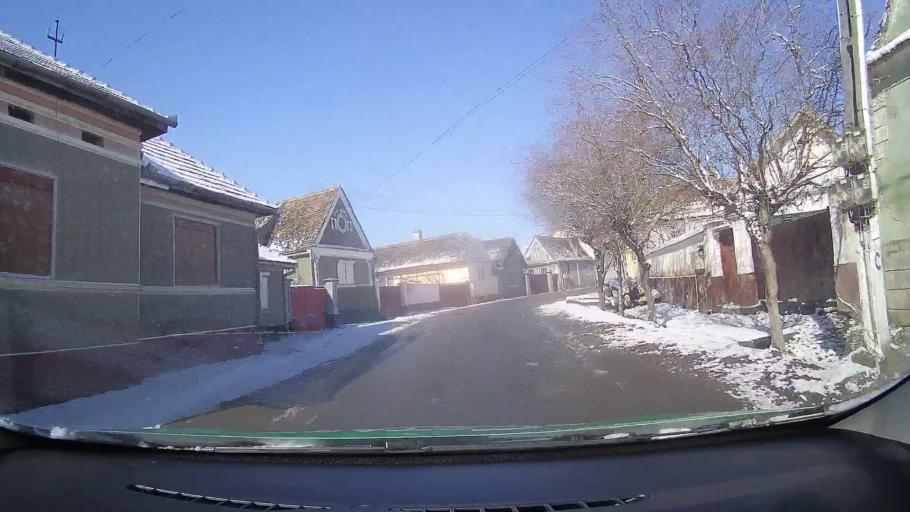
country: RO
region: Sibiu
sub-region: Comuna Avrig
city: Avrig
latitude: 45.7581
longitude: 24.3899
